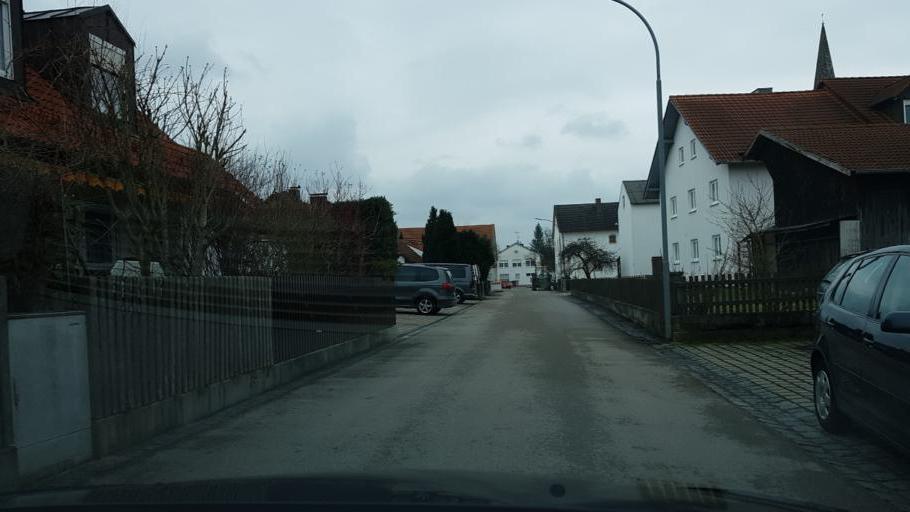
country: DE
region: Bavaria
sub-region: Upper Bavaria
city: Mammendorf
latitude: 48.2069
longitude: 11.1562
